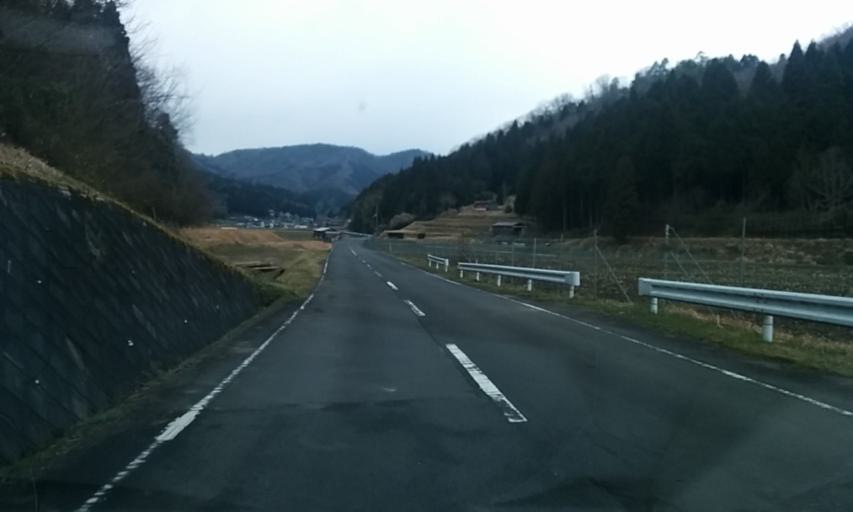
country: JP
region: Kyoto
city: Kameoka
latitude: 35.1193
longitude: 135.4204
